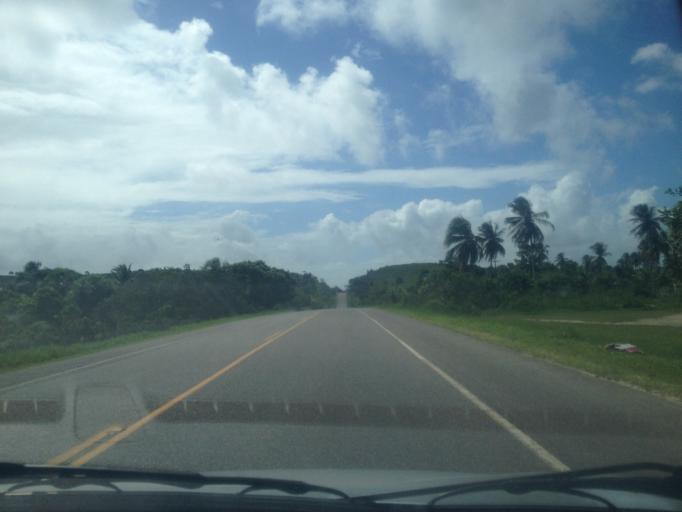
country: BR
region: Bahia
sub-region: Conde
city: Conde
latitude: -11.7854
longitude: -37.6175
